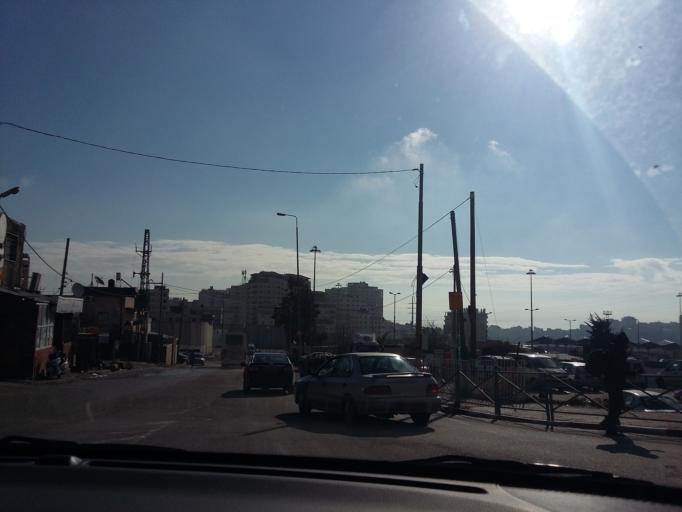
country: PS
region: West Bank
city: `Anata
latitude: 31.8104
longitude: 35.2406
